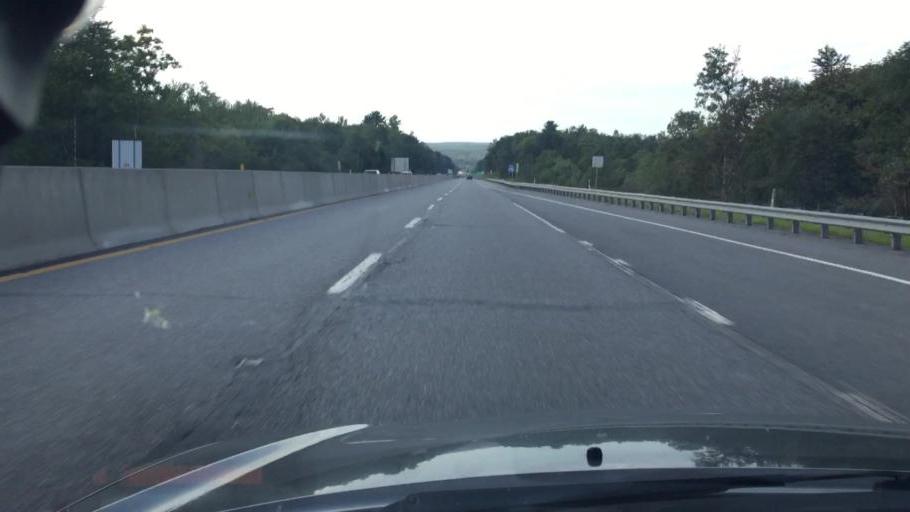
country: US
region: Pennsylvania
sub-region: Carbon County
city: Towamensing Trails
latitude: 40.9900
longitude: -75.6312
